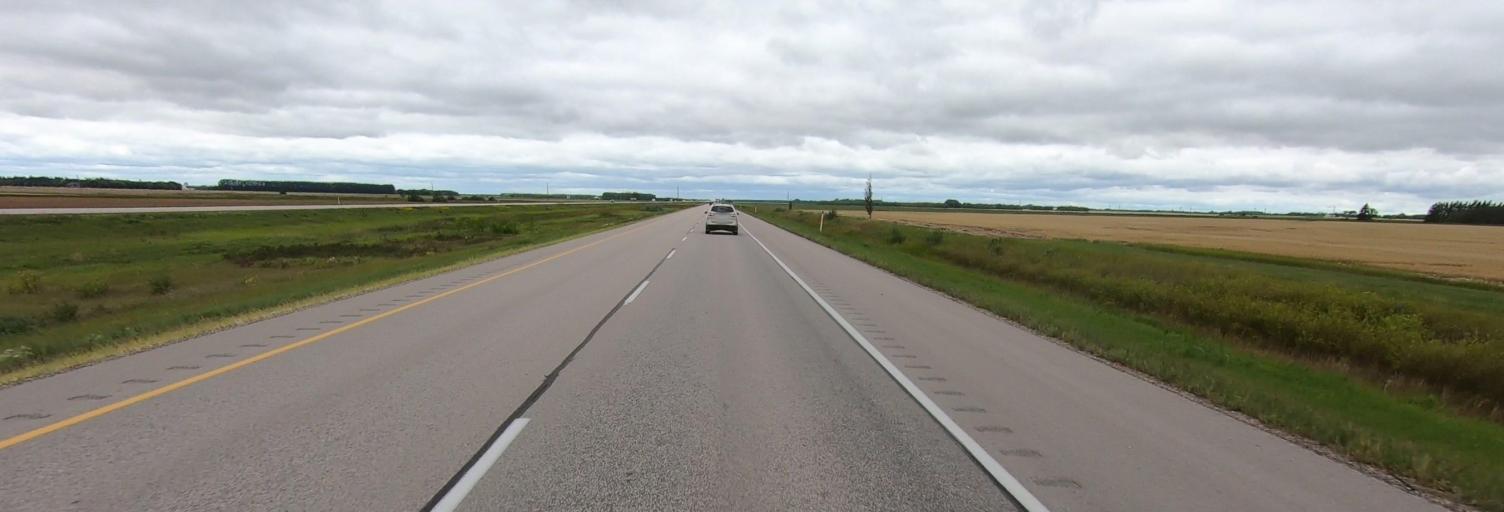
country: CA
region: Manitoba
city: Portage la Prairie
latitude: 49.9399
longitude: -97.9346
